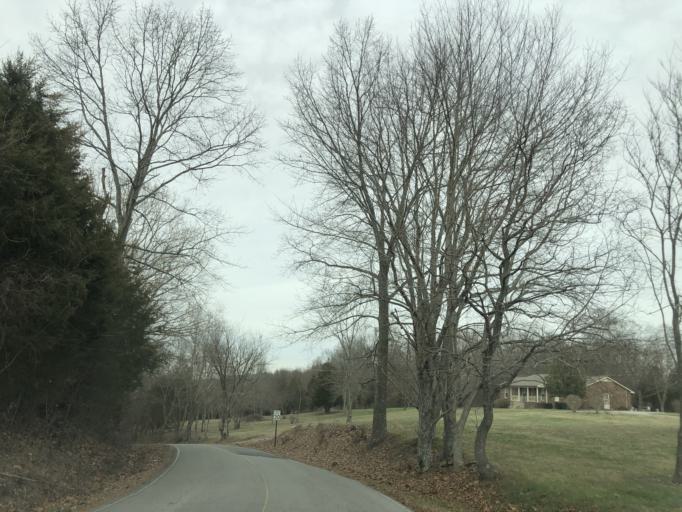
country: US
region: Tennessee
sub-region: Robertson County
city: Greenbrier
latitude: 36.4697
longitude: -86.7982
